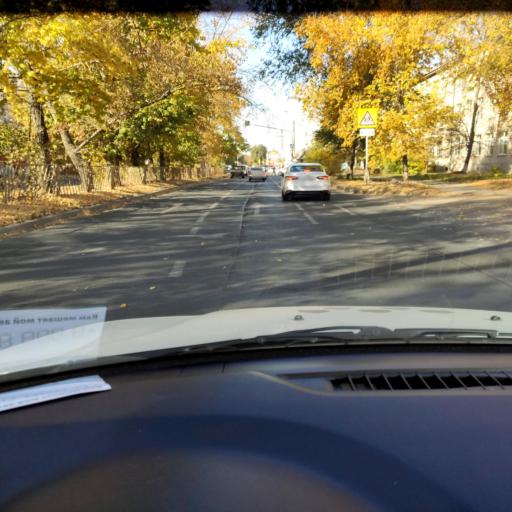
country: RU
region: Samara
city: Tol'yatti
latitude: 53.5177
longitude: 49.4270
